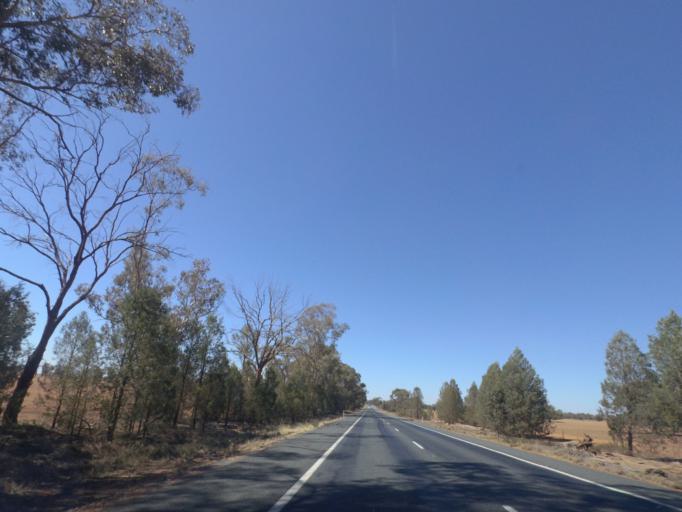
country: AU
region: New South Wales
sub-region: Bland
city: West Wyalong
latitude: -34.1849
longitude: 147.1127
